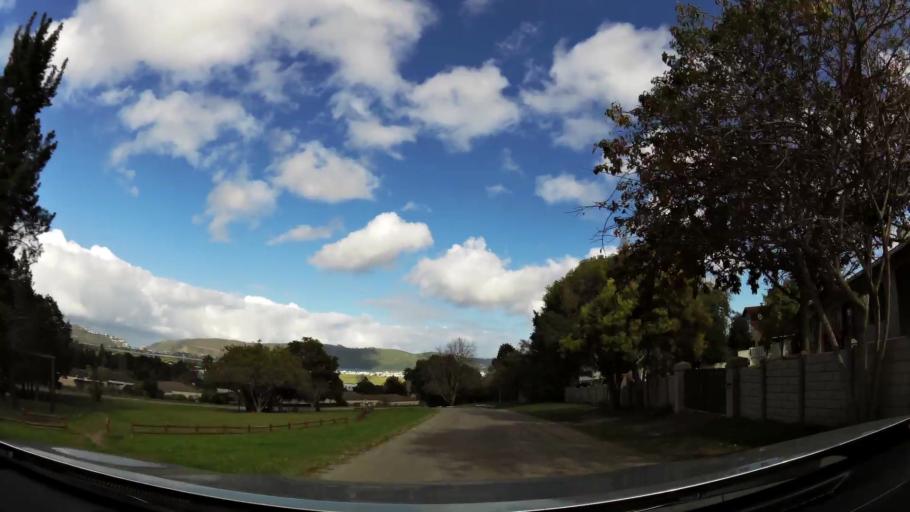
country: ZA
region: Western Cape
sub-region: Eden District Municipality
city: Knysna
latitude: -34.0382
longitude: 23.0723
